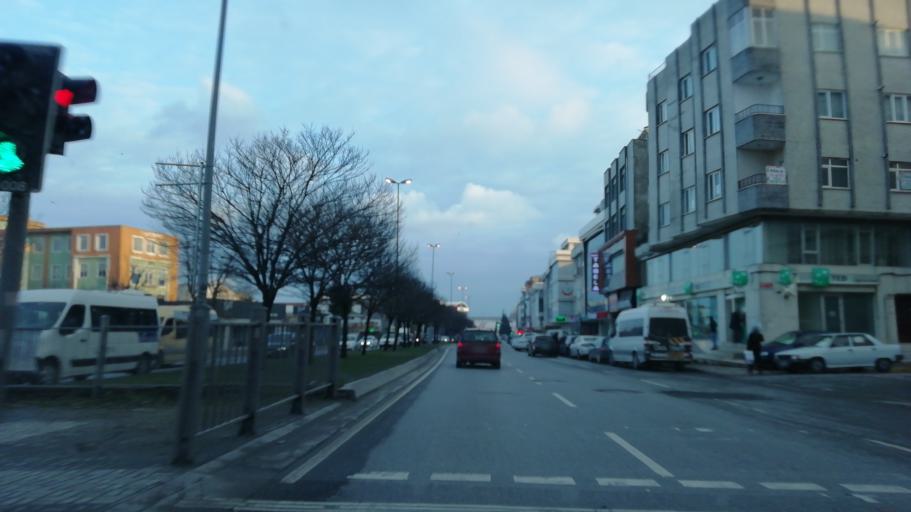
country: TR
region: Istanbul
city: Yakuplu
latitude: 41.0027
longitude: 28.7099
